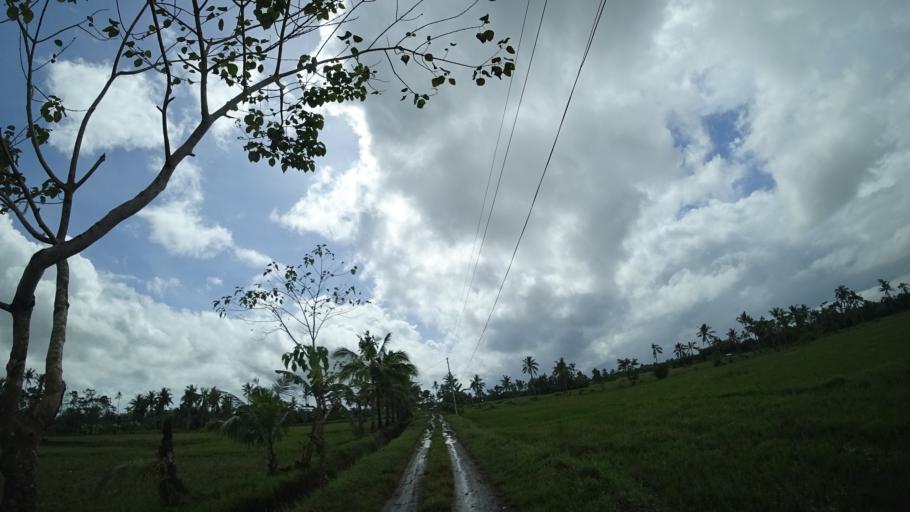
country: PH
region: Eastern Visayas
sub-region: Province of Leyte
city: Cabacungan
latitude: 10.9161
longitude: 124.9814
